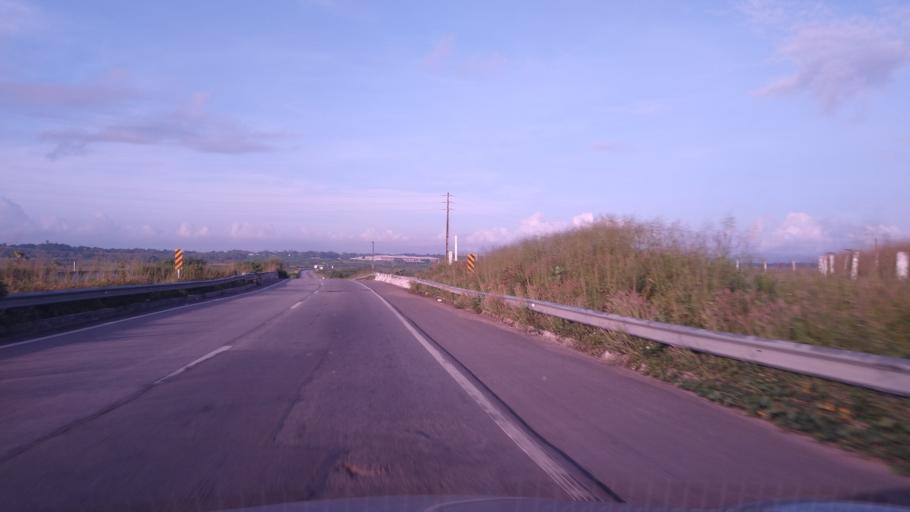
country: BR
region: Ceara
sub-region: Pacajus
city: Pacajus
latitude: -4.1549
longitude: -38.4814
